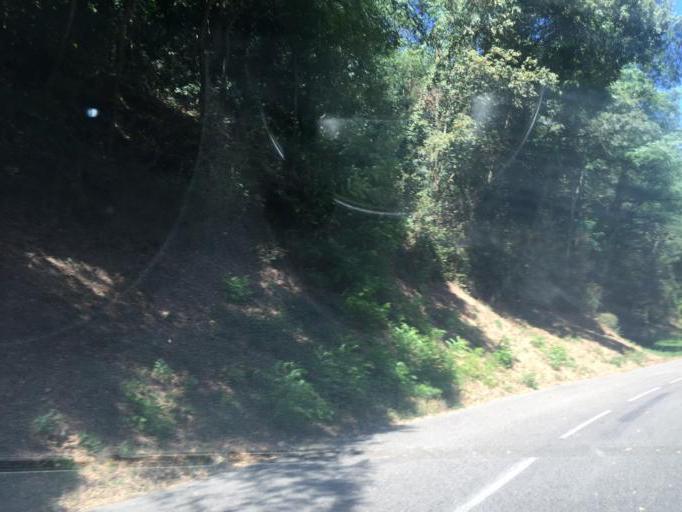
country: FR
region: Rhone-Alpes
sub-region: Departement de l'Ain
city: Saint-Maurice-de-Beynost
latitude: 45.8391
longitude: 4.9751
